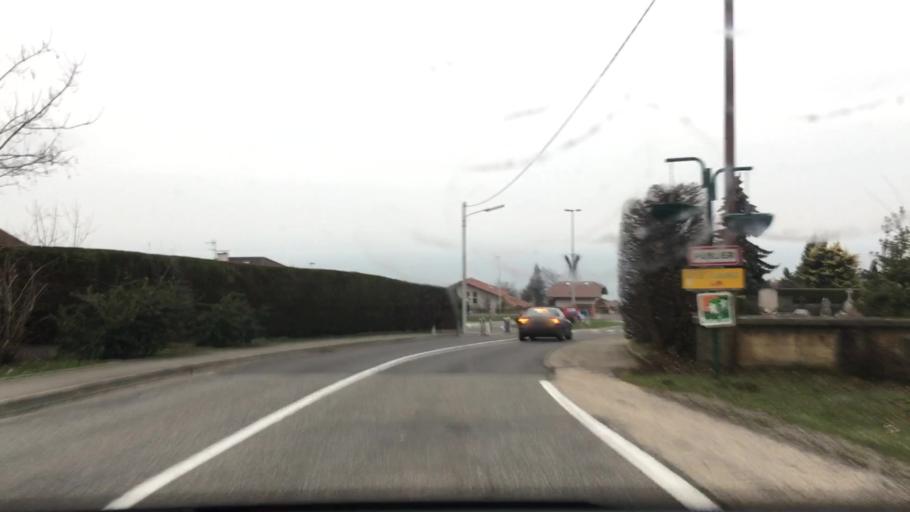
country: FR
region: Rhone-Alpes
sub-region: Departement de la Haute-Savoie
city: Publier
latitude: 46.3864
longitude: 6.5466
